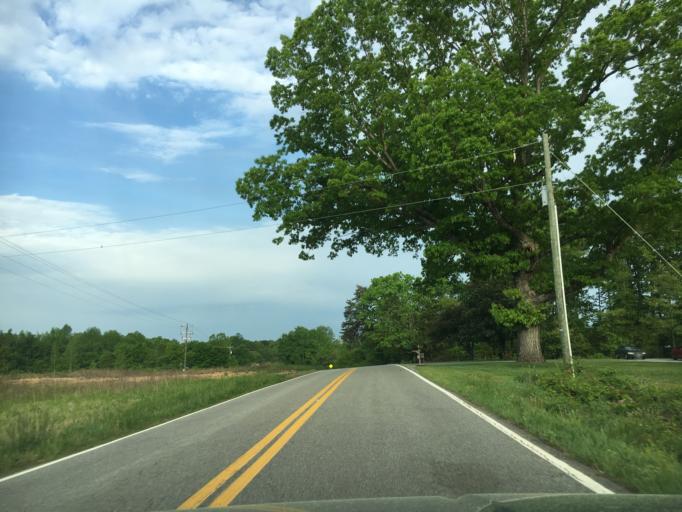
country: US
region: Virginia
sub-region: Halifax County
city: Halifax
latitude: 36.8896
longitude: -78.7997
